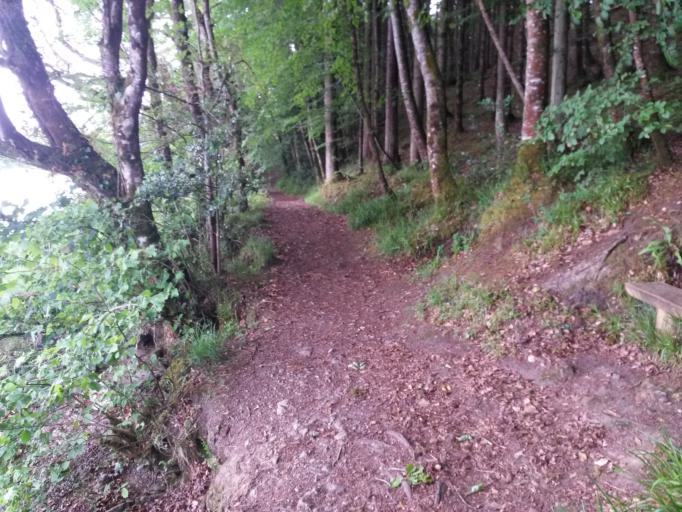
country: IE
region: Connaught
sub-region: Sligo
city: Sligo
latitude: 54.2393
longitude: -8.4256
